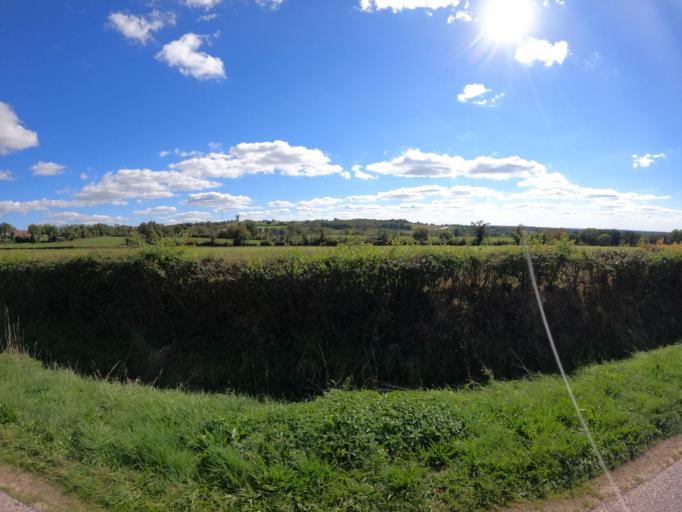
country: FR
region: Auvergne
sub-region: Departement de l'Allier
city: Buxieres-les-Mines
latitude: 46.4053
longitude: 3.0442
